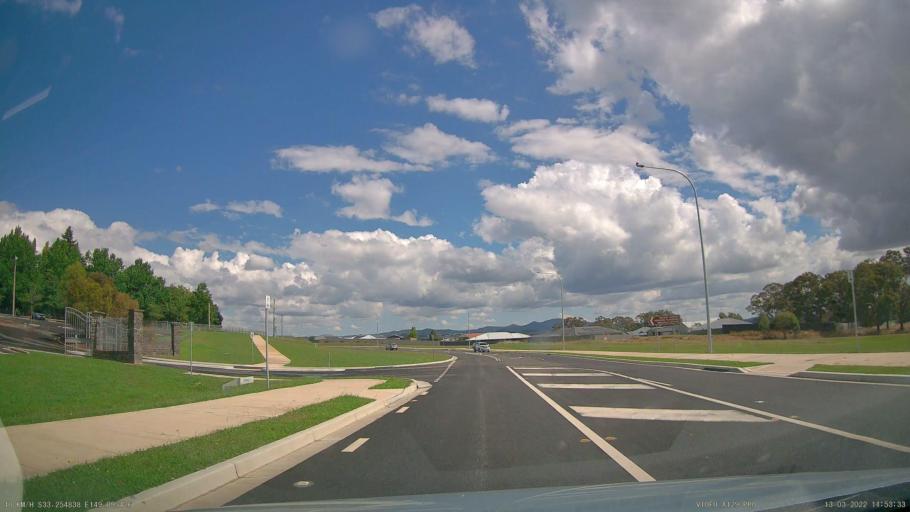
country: AU
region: New South Wales
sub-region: Orange Municipality
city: Orange
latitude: -33.2550
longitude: 149.0954
